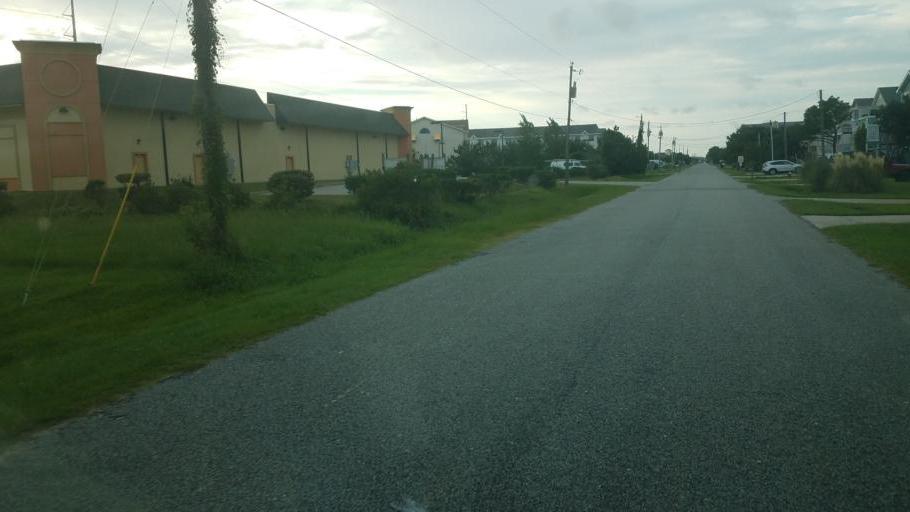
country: US
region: North Carolina
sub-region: Dare County
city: Kill Devil Hills
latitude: 36.0029
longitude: -75.6533
